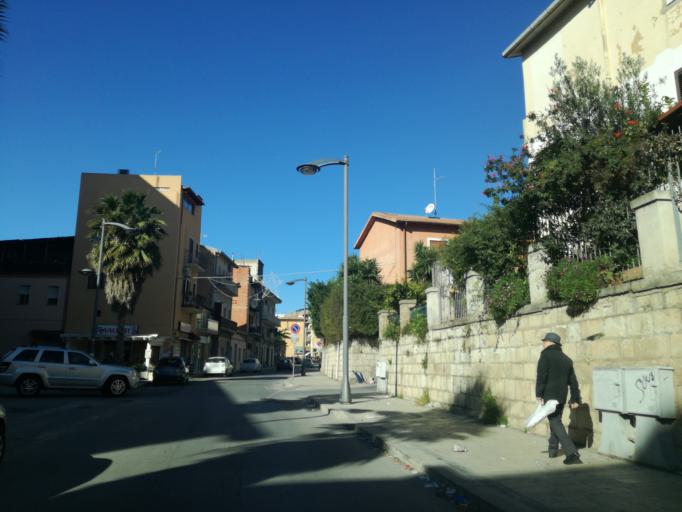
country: IT
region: Sicily
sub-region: Provincia di Caltanissetta
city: Gela
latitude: 37.0720
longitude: 14.2358
